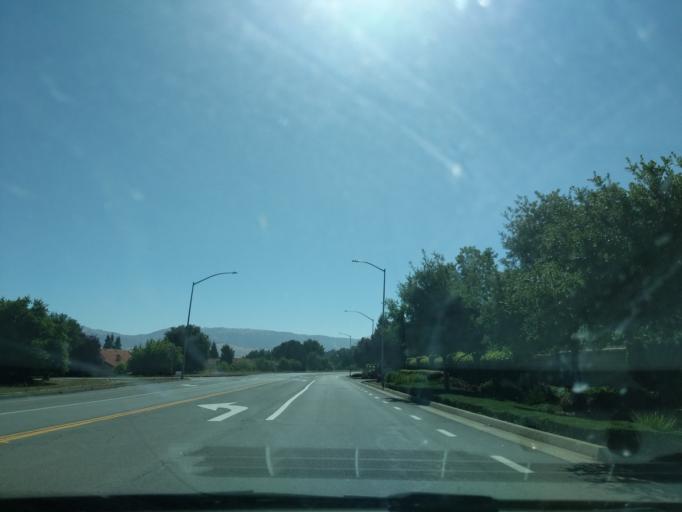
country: US
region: California
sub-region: Santa Clara County
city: San Martin
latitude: 37.0925
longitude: -121.6434
